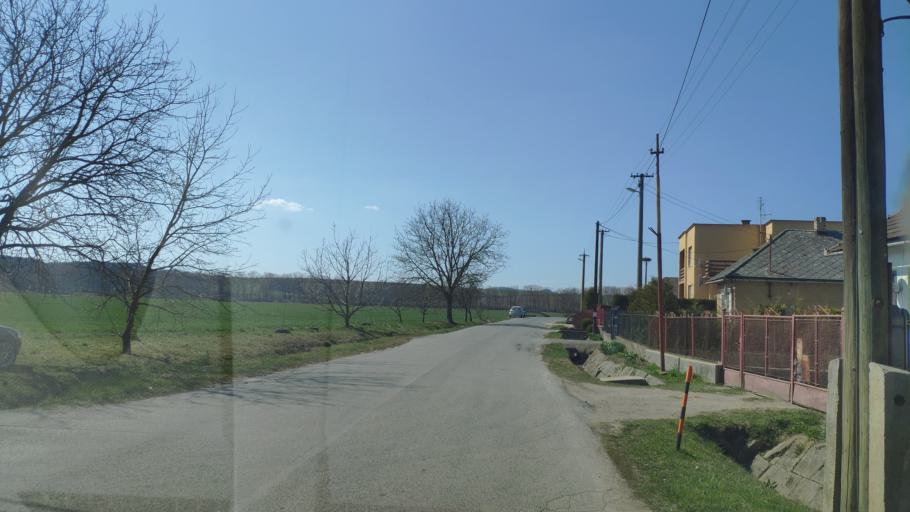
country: SK
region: Kosicky
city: Moldava nad Bodvou
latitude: 48.5782
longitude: 20.9491
